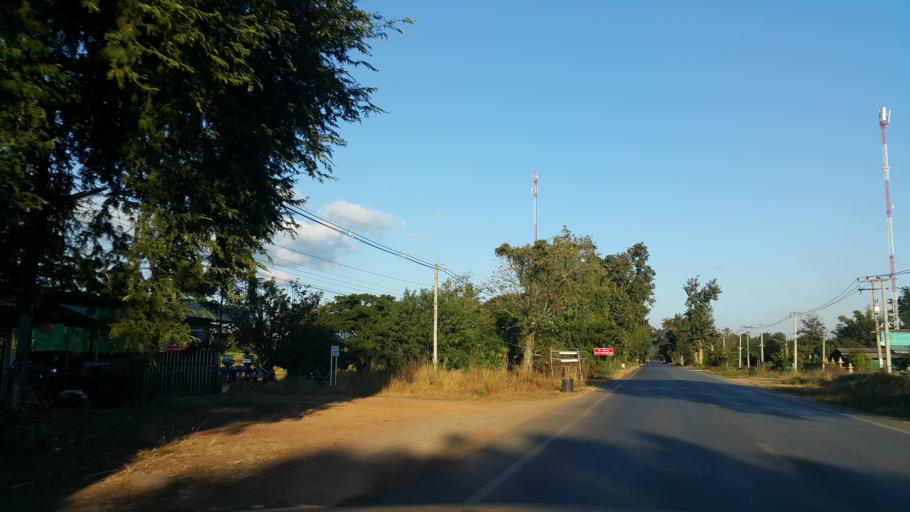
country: TH
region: Sukhothai
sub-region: Amphoe Si Satchanalai
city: Si Satchanalai
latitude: 17.5496
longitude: 99.8576
